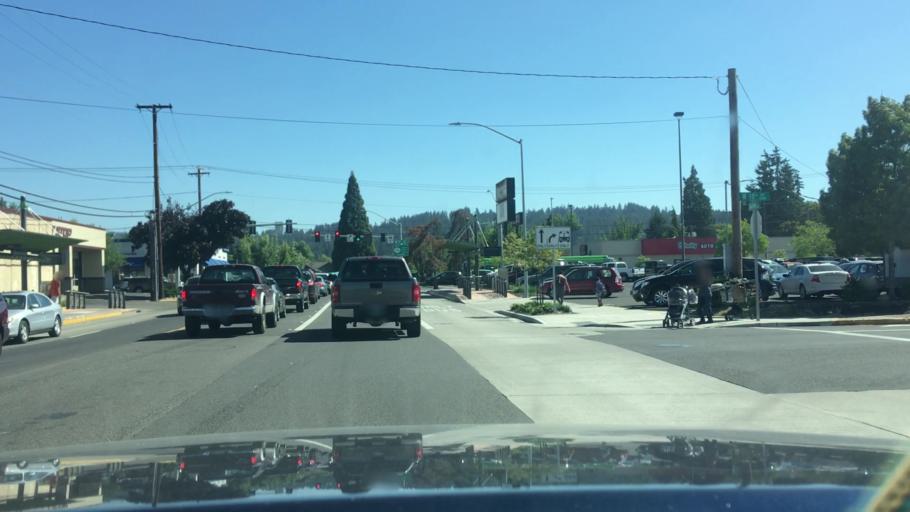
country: US
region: Oregon
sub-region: Lane County
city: Eugene
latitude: 44.0486
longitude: -123.1231
